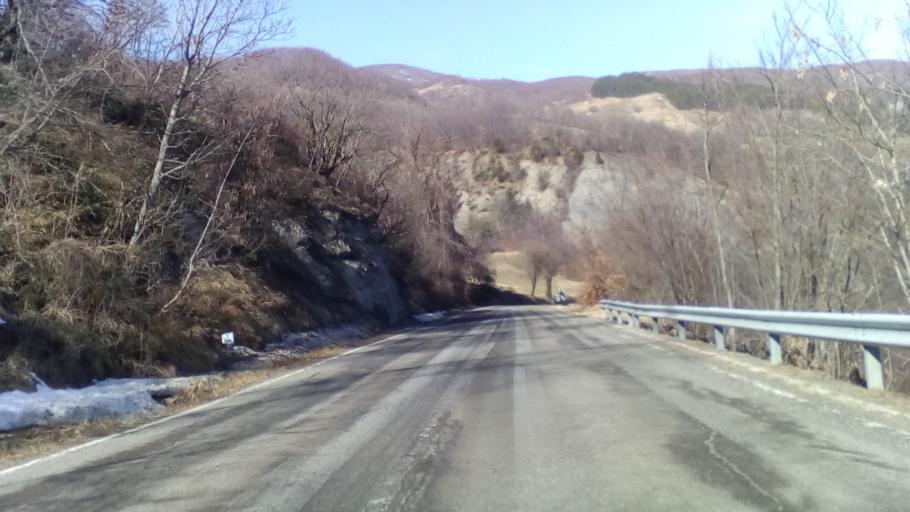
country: IT
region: Emilia-Romagna
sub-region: Provincia di Modena
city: Riolunato
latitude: 44.2280
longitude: 10.6288
